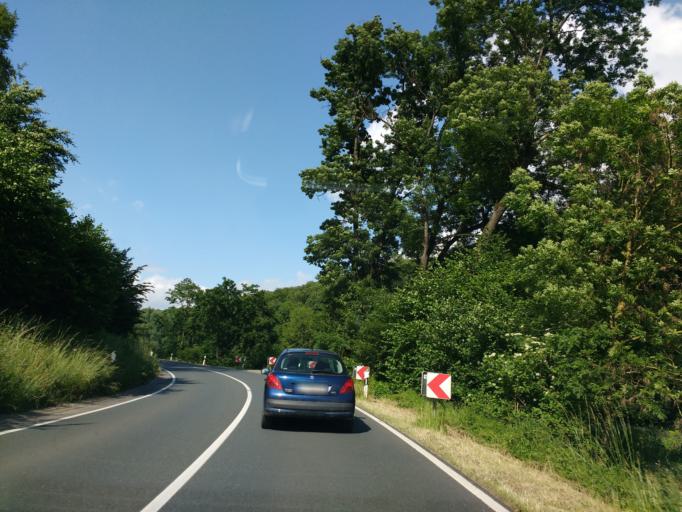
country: DE
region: North Rhine-Westphalia
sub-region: Regierungsbezirk Detmold
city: Vlotho
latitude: 52.1380
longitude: 8.9481
